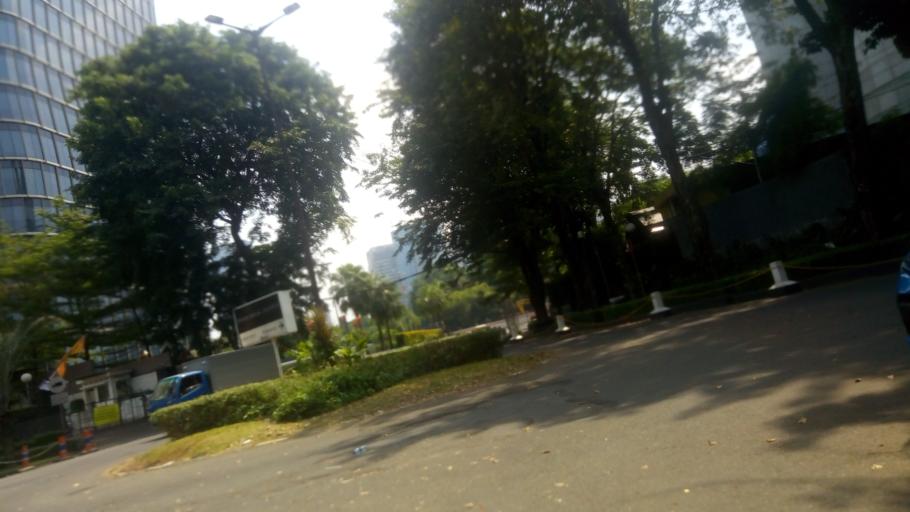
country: ID
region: Jakarta Raya
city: Jakarta
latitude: -6.2358
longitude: 106.8301
